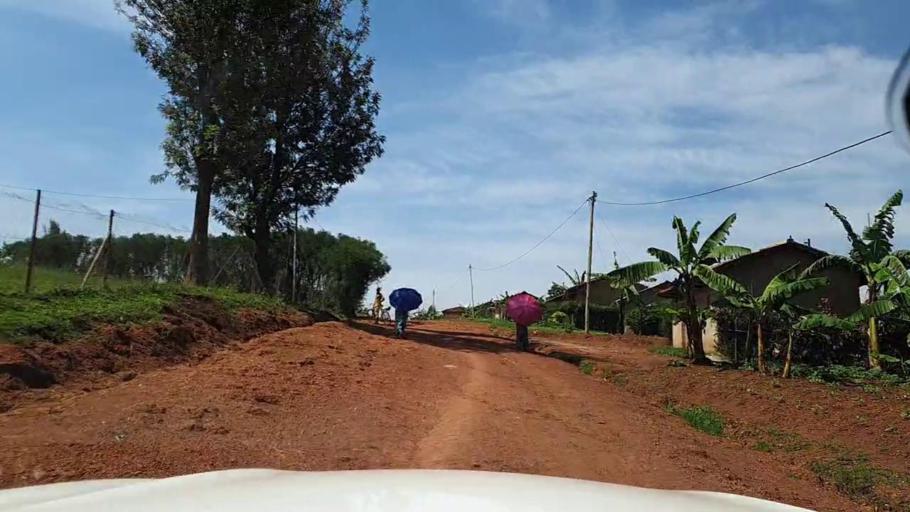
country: RW
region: Southern Province
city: Butare
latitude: -2.7178
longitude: 29.8388
